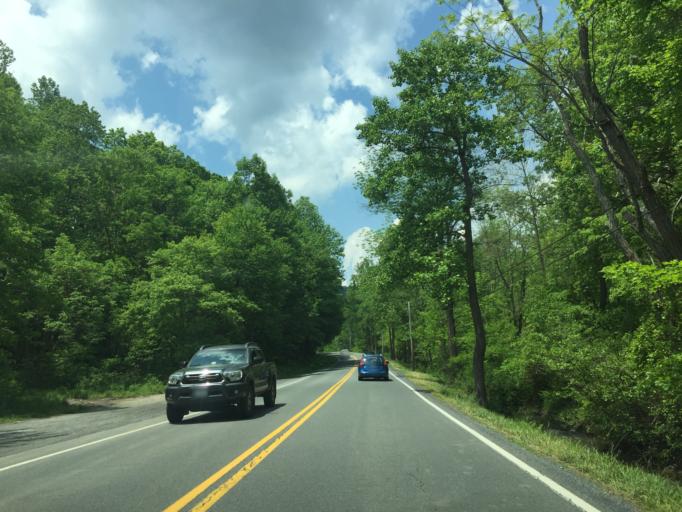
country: US
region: Virginia
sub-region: Frederick County
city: Shawnee Land
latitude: 39.0993
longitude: -78.4733
